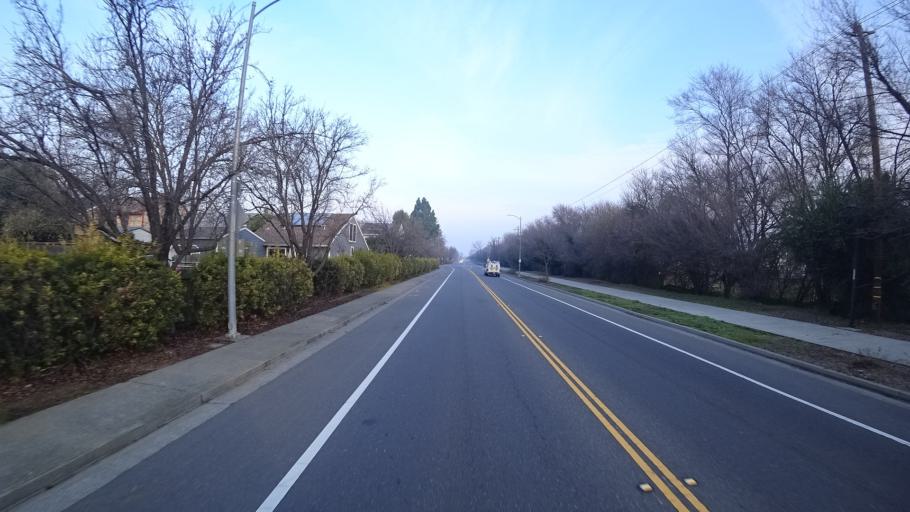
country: US
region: California
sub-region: Yolo County
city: Davis
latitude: 38.5651
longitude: -121.7449
